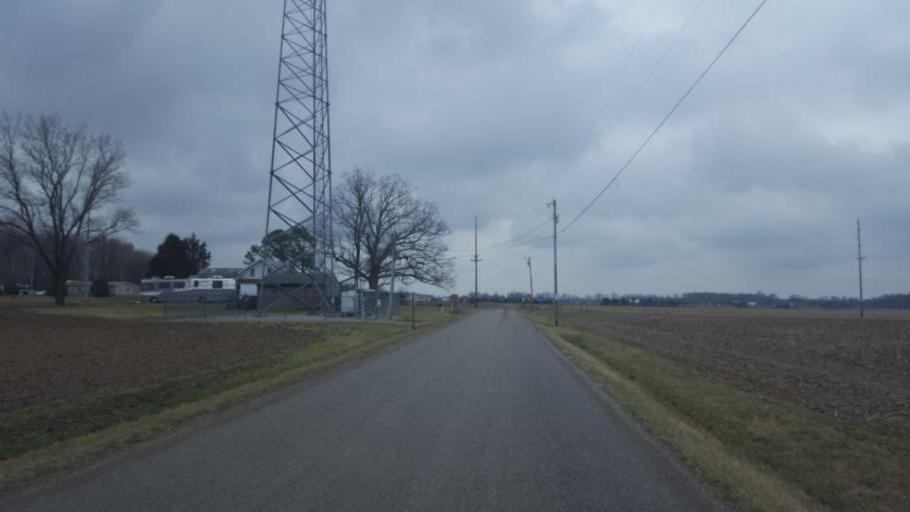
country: US
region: Ohio
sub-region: Delaware County
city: Ashley
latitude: 40.3600
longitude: -82.8554
